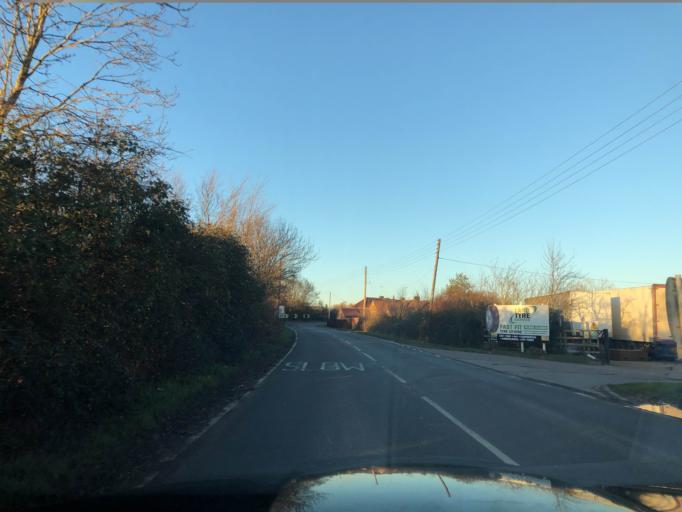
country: GB
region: England
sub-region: Warwickshire
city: Harbury
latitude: 52.2086
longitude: -1.4397
